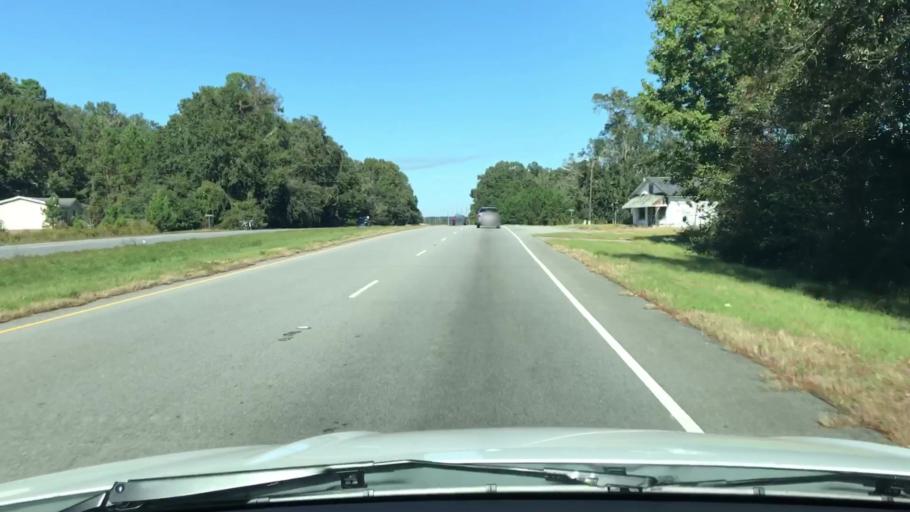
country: US
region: South Carolina
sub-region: Beaufort County
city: Laurel Bay
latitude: 32.5252
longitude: -80.7492
